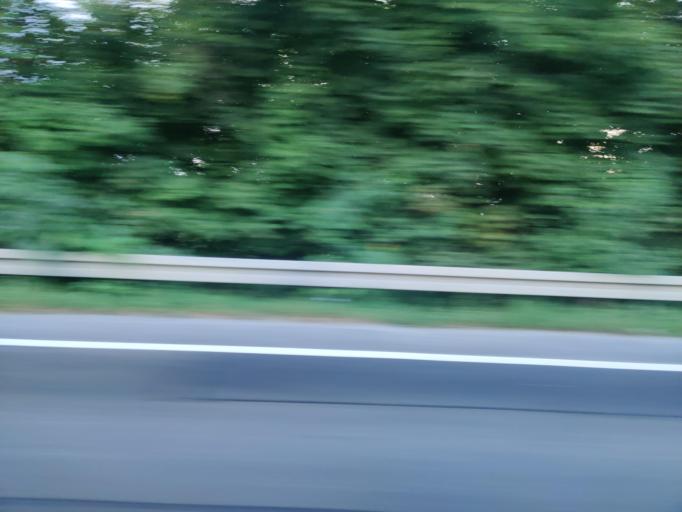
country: PL
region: Greater Poland Voivodeship
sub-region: Konin
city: Konin
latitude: 52.2068
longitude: 18.2666
